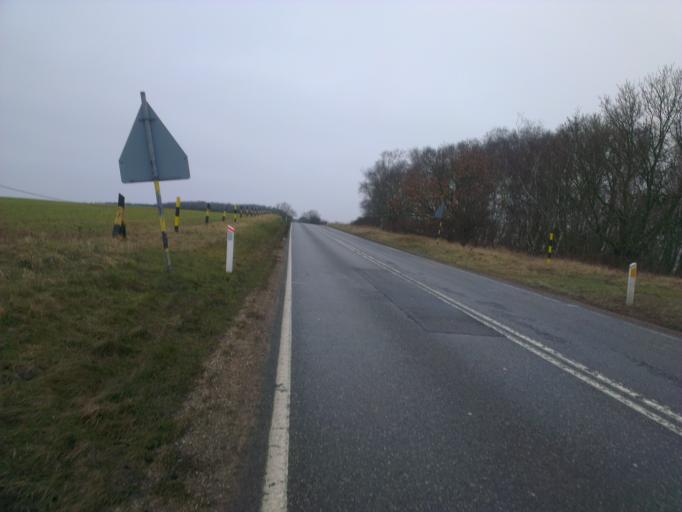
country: DK
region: Capital Region
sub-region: Frederikssund Kommune
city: Jaegerspris
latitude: 55.8675
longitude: 11.9655
